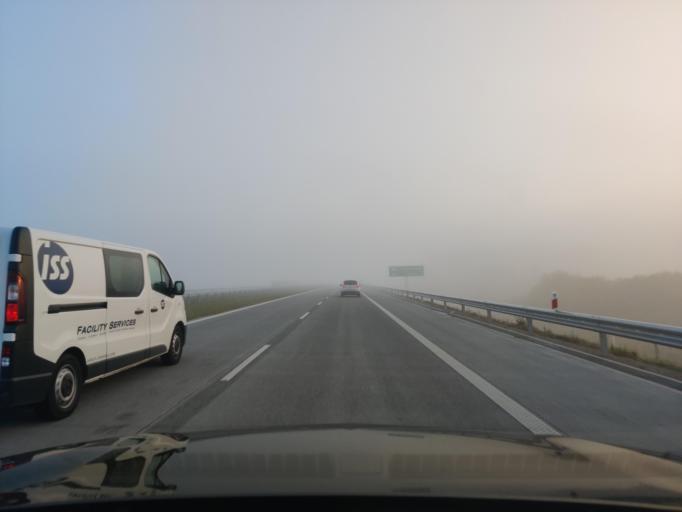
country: PL
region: Masovian Voivodeship
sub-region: Powiat mlawski
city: Strzegowo
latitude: 52.9666
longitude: 20.3166
